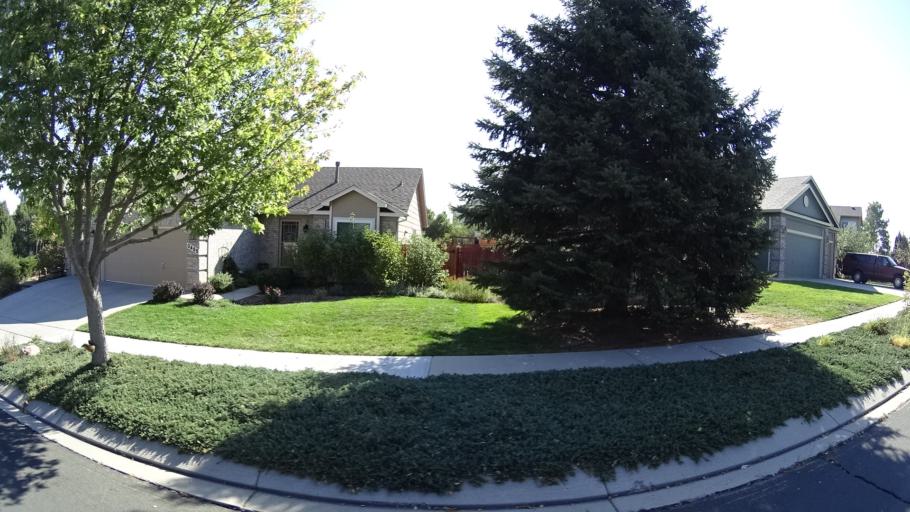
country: US
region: Colorado
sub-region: El Paso County
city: Cimarron Hills
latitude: 38.8826
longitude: -104.7042
